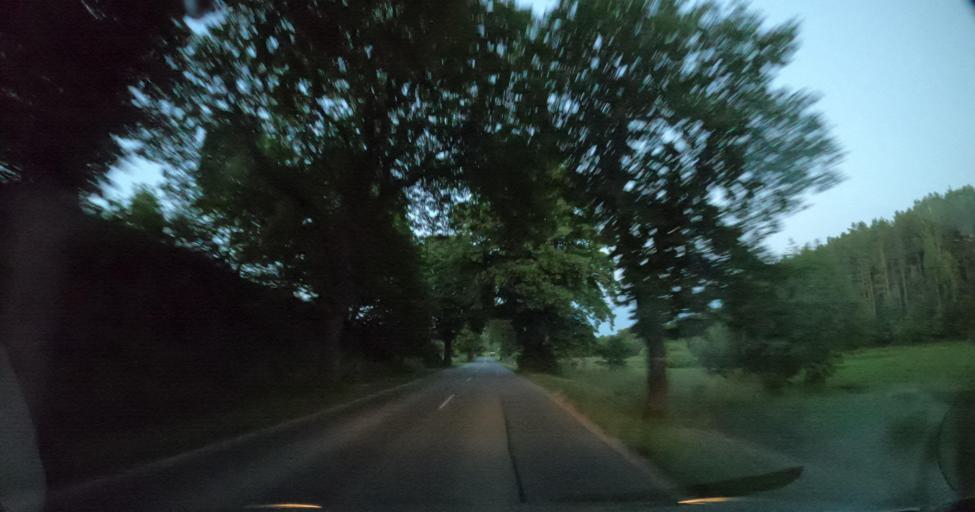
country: PL
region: Pomeranian Voivodeship
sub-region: Powiat wejherowski
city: Koleczkowo
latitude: 54.4689
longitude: 18.3038
